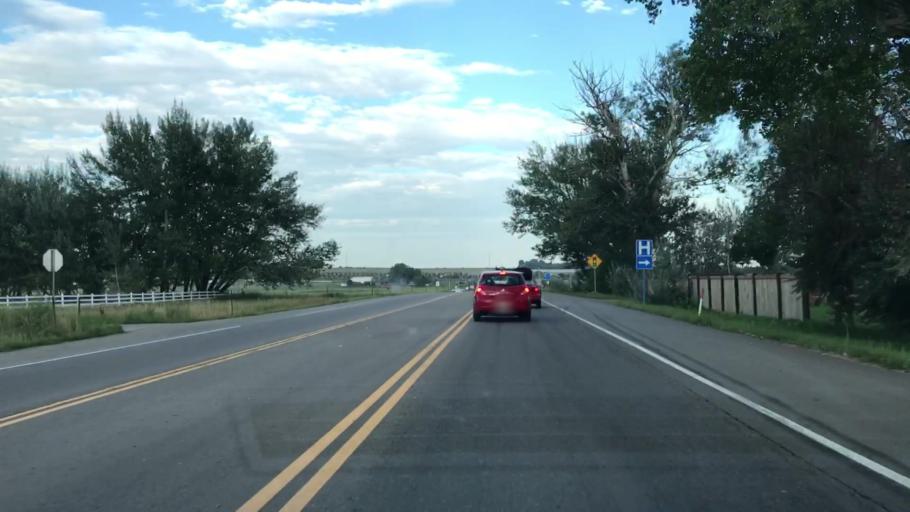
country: US
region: Colorado
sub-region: Boulder County
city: Longmont
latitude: 40.2036
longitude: -105.0597
